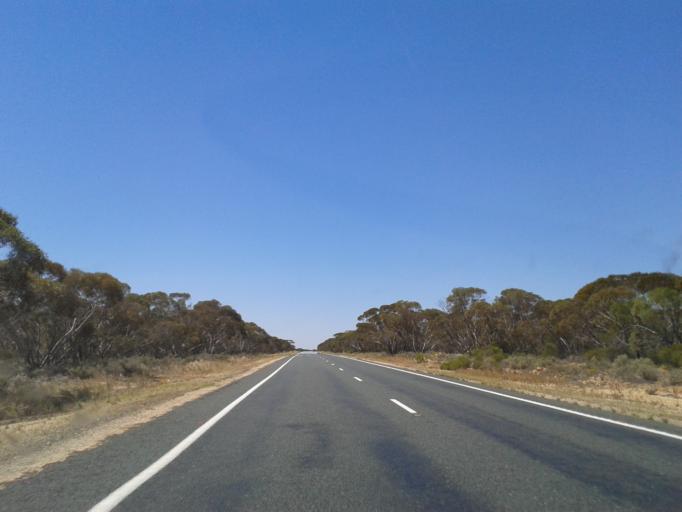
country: AU
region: New South Wales
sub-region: Wentworth
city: Gol Gol
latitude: -34.4488
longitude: 142.5037
